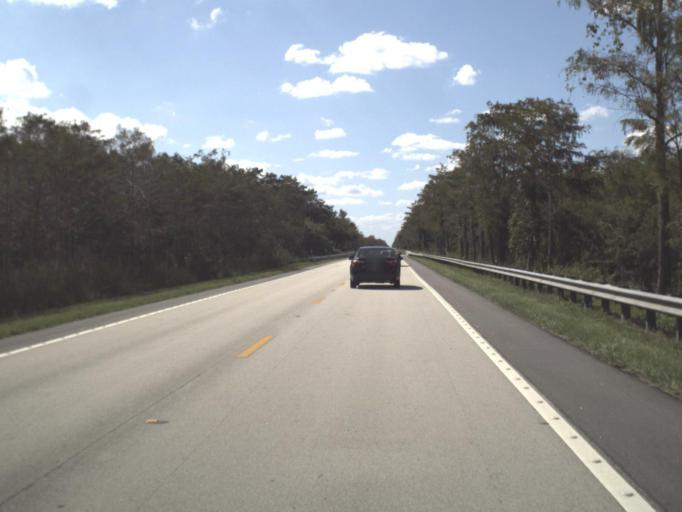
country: US
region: Florida
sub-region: Miami-Dade County
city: Kendall West
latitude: 25.8491
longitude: -80.9565
